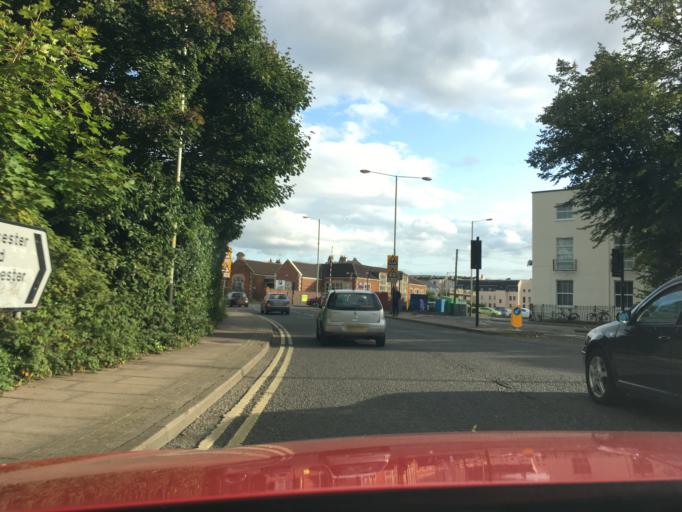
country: GB
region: England
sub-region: Gloucestershire
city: Cheltenham
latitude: 51.8995
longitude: -2.0692
